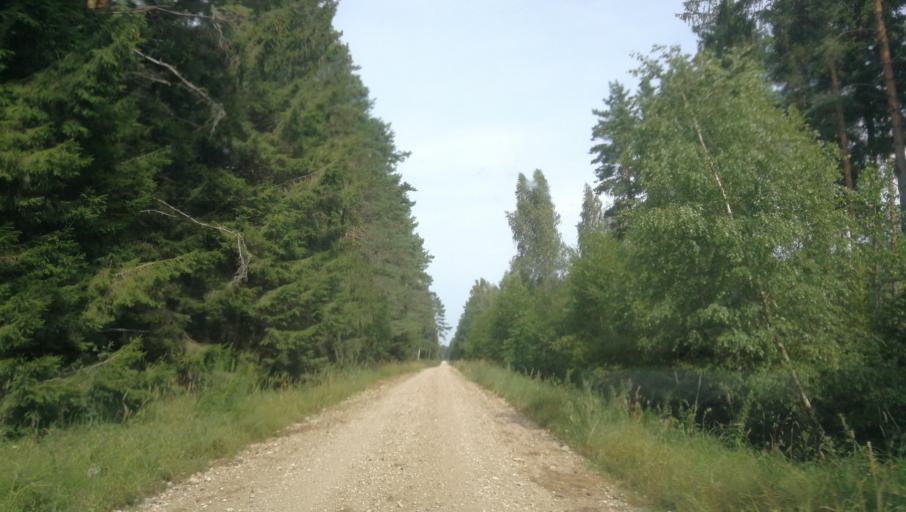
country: LV
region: Pavilostas
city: Pavilosta
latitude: 56.8041
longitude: 21.3382
